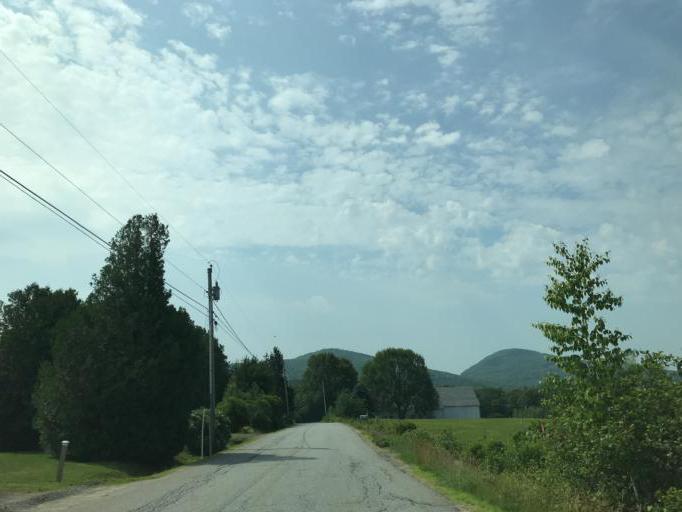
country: US
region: Maine
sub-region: Knox County
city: Hope
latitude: 44.2140
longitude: -69.1703
